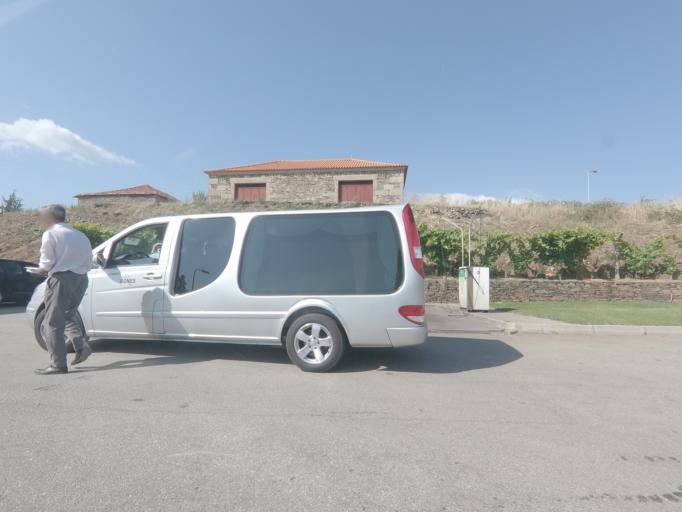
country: PT
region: Vila Real
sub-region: Sabrosa
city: Sabrosa
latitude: 41.2637
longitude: -7.5896
